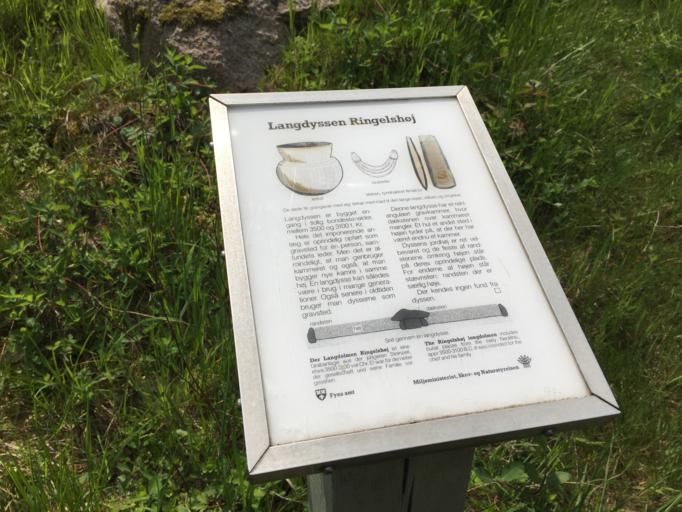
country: DK
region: South Denmark
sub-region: Langeland Kommune
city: Rudkobing
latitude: 54.9786
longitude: 10.7984
